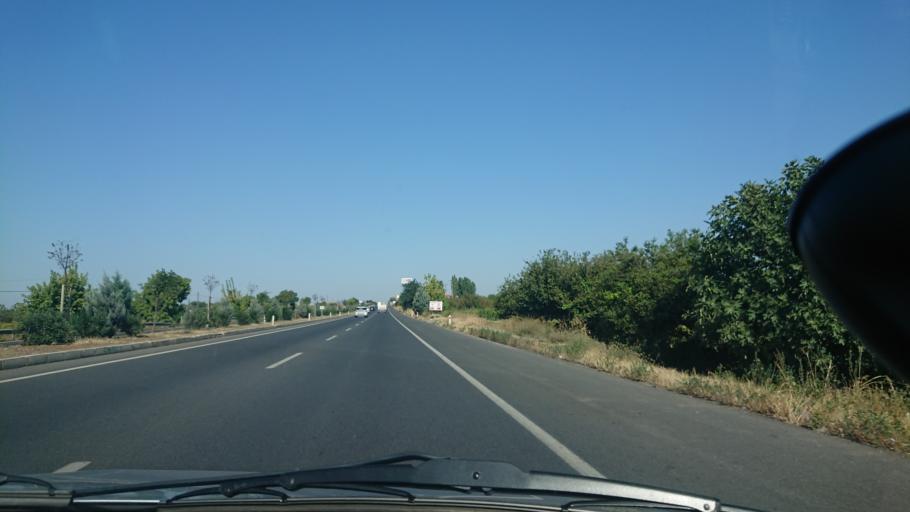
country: TR
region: Manisa
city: Ahmetli
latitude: 38.4950
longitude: 27.8561
